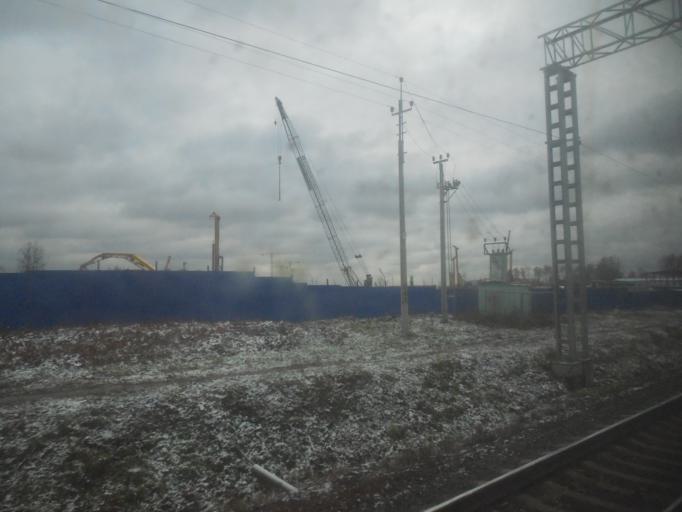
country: RU
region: Moskovskaya
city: Novoivanovskoye
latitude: 55.7003
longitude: 37.3430
